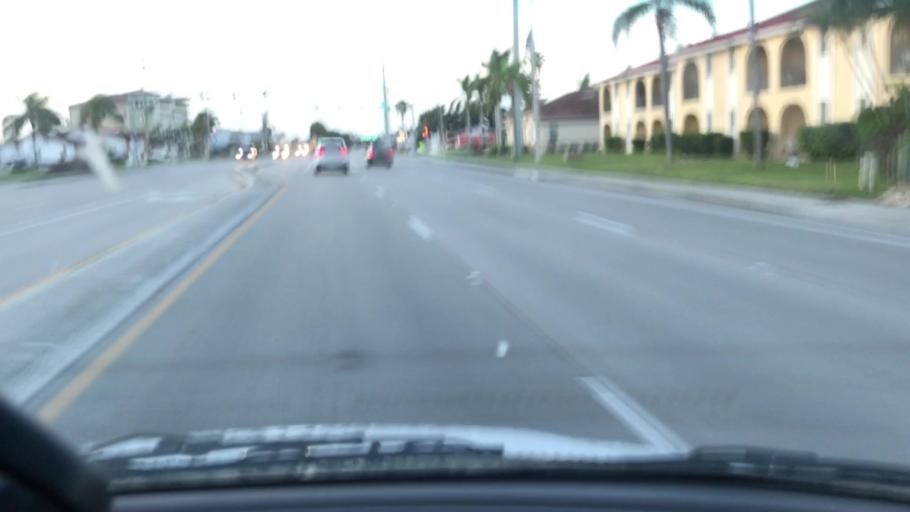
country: US
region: Florida
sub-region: Lee County
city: Cape Coral
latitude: 26.5857
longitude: -81.9420
